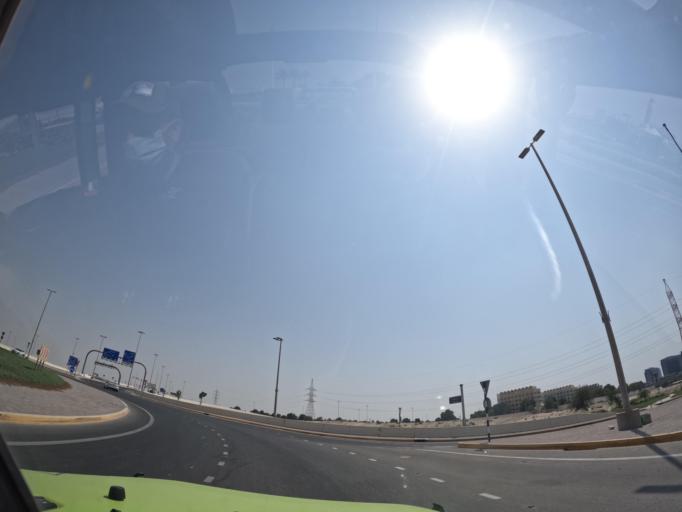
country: AE
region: Abu Dhabi
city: Abu Dhabi
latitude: 24.3295
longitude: 54.6205
